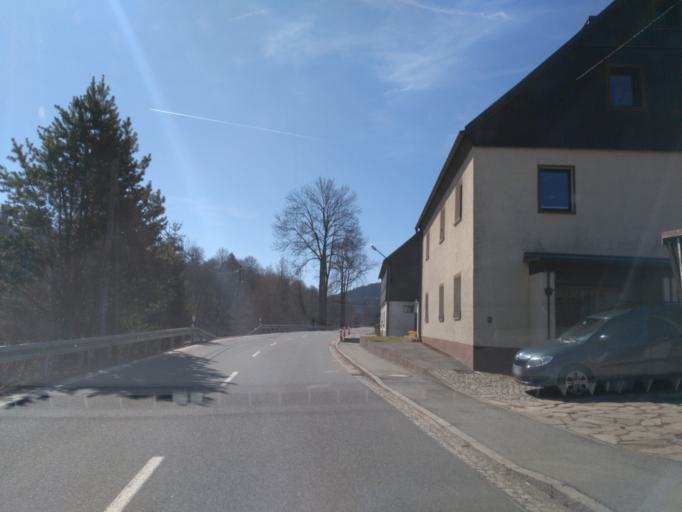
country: CZ
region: Ustecky
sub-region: Okres Chomutov
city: Vejprty
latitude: 50.4718
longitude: 13.0191
